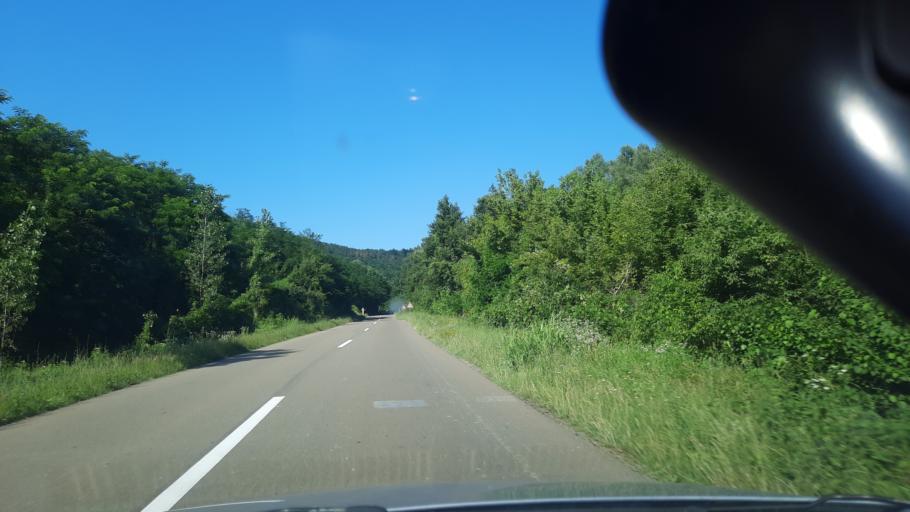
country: RS
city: Turija
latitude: 44.5241
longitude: 21.6096
